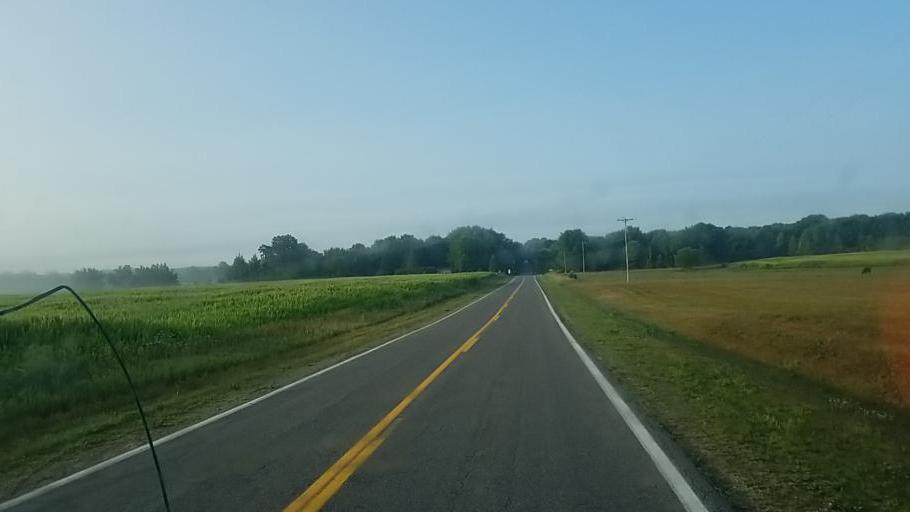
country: US
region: Michigan
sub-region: Muskegon County
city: Twin Lake
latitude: 43.4418
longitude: -86.0792
